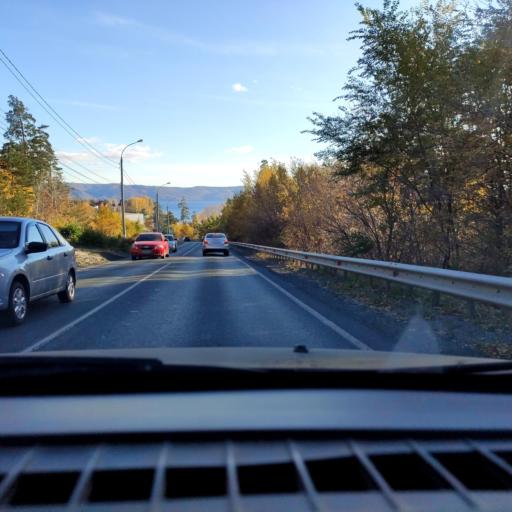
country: RU
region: Samara
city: Tol'yatti
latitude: 53.4798
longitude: 49.3225
